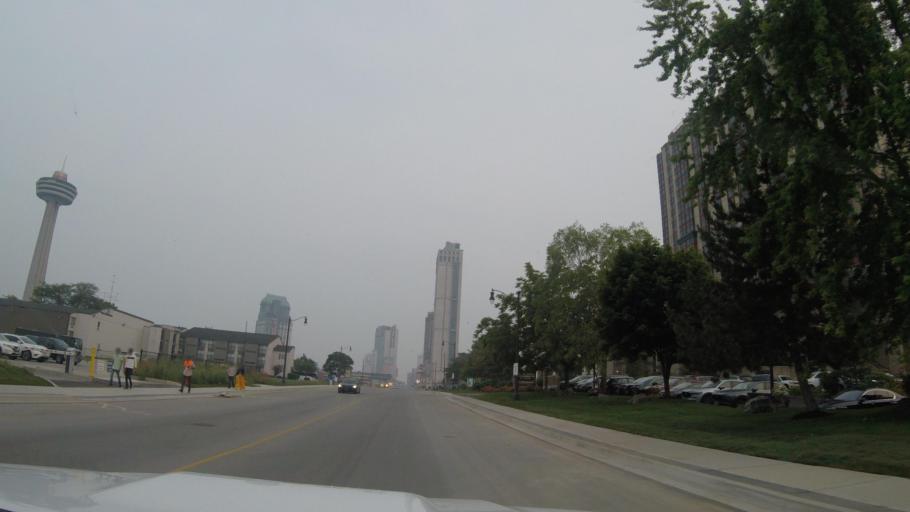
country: CA
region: Ontario
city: Niagara Falls
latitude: 43.0880
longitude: -79.0833
